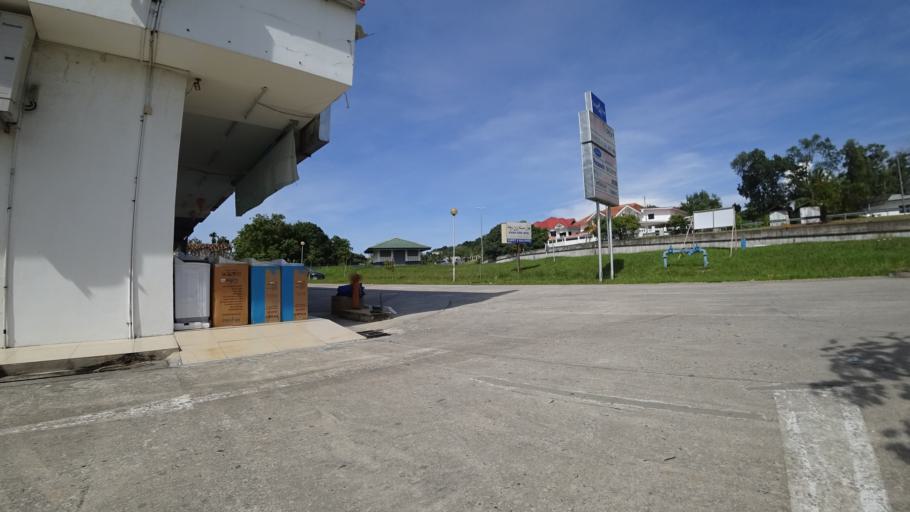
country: BN
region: Brunei and Muara
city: Bandar Seri Begawan
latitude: 4.8831
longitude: 114.8579
